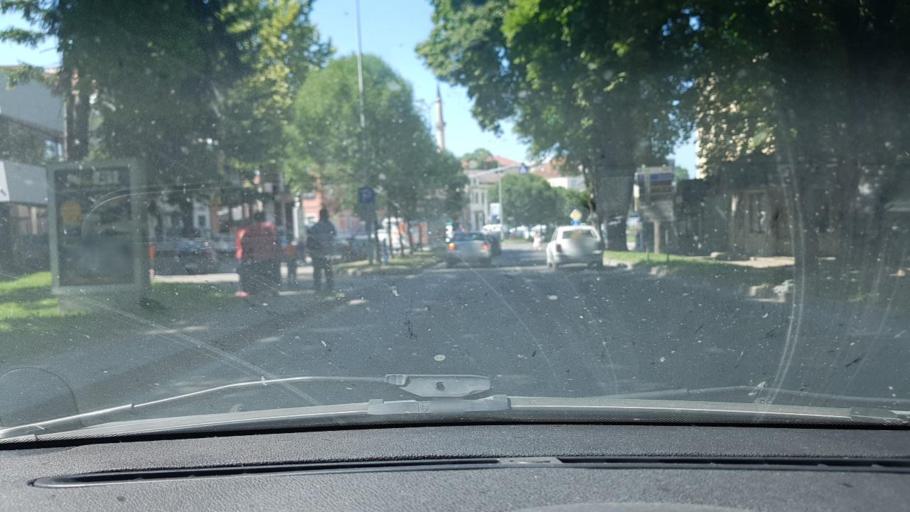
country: BA
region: Federation of Bosnia and Herzegovina
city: Bihac
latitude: 44.8144
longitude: 15.8706
